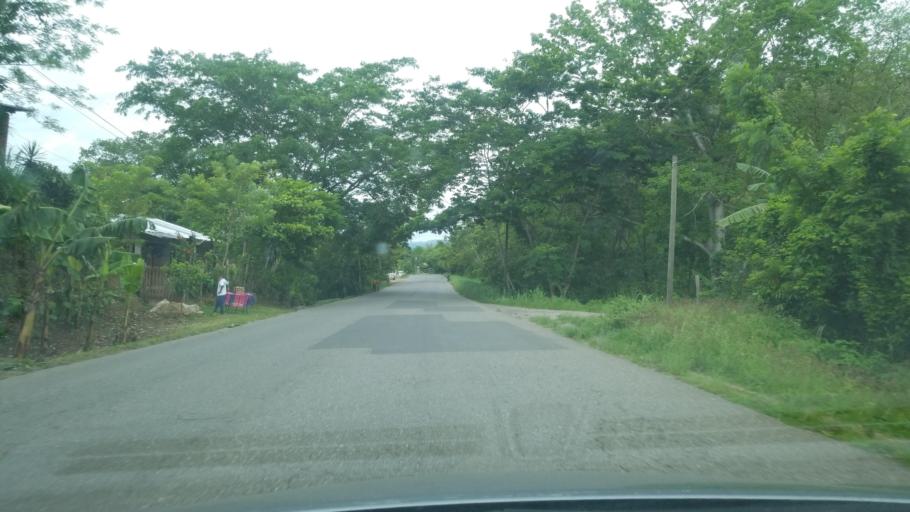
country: HN
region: Santa Barbara
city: La Flecha
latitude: 15.2999
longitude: -88.4801
